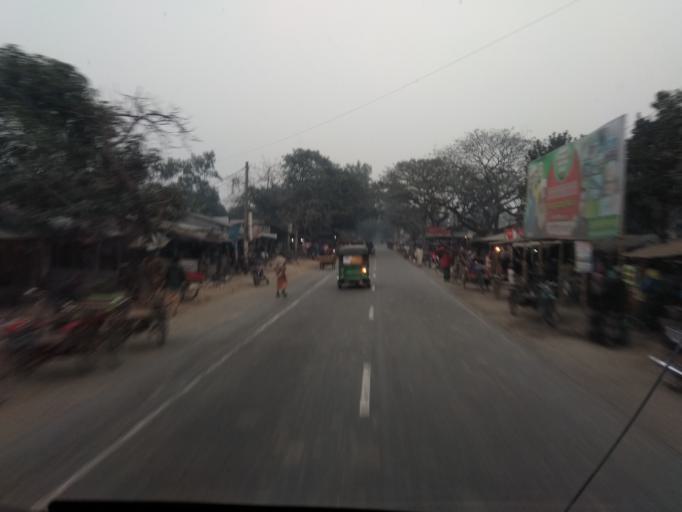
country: BD
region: Rajshahi
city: Bogra
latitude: 24.6783
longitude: 89.2851
